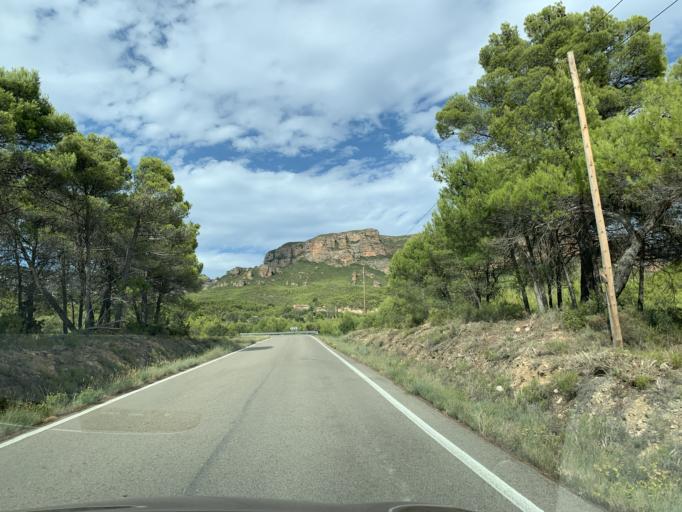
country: ES
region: Aragon
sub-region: Provincia de Zaragoza
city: Santa Eulalia de Gallego
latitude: 42.3259
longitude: -0.7224
